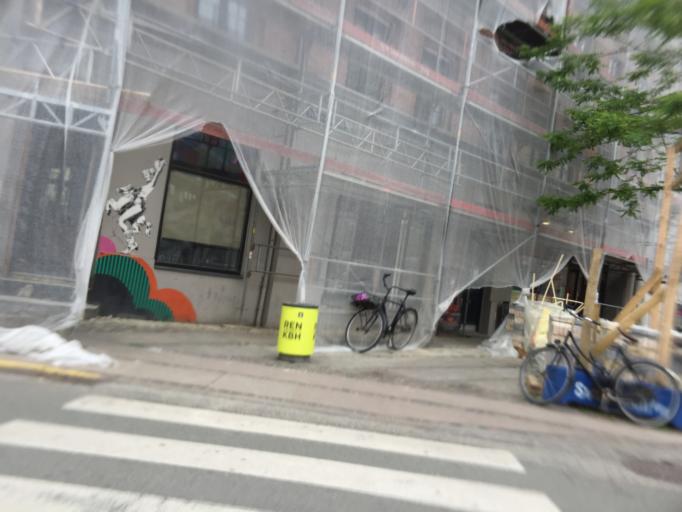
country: DK
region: Capital Region
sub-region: Frederiksberg Kommune
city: Frederiksberg
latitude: 55.6694
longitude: 12.5454
